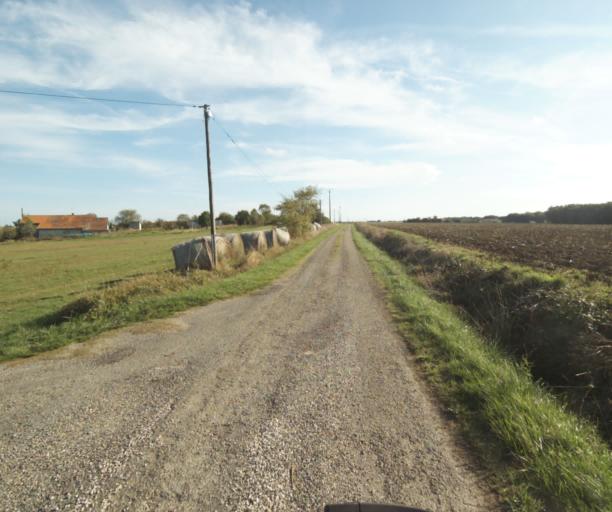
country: FR
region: Midi-Pyrenees
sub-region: Departement du Tarn-et-Garonne
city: Finhan
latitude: 43.9235
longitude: 1.1254
